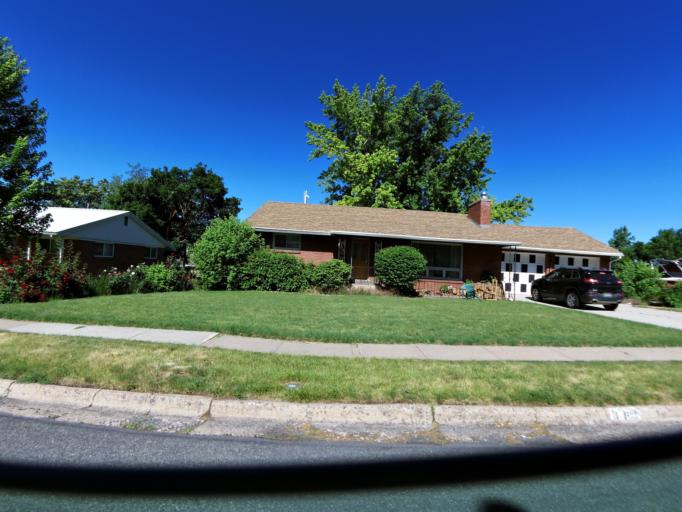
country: US
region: Utah
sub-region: Weber County
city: South Ogden
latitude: 41.2067
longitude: -111.9453
